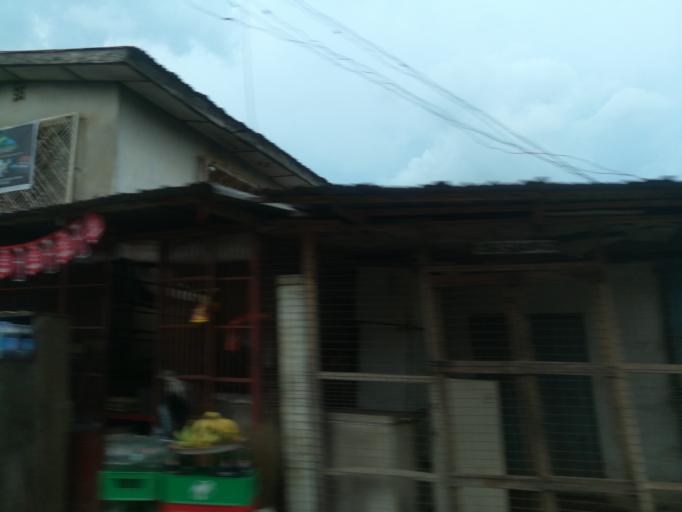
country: NG
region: Oyo
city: Moniya
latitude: 7.4547
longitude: 3.9100
